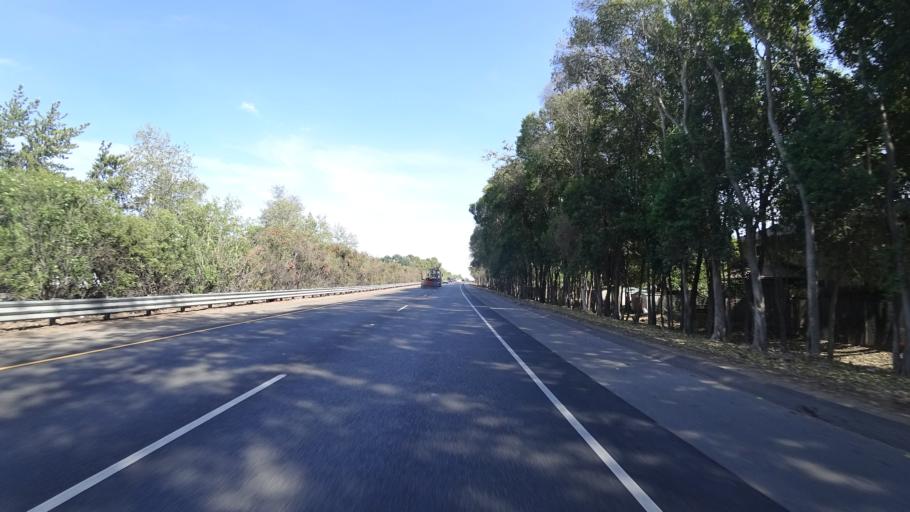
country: US
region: California
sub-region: Butte County
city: Chico
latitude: 39.7506
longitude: -121.8390
